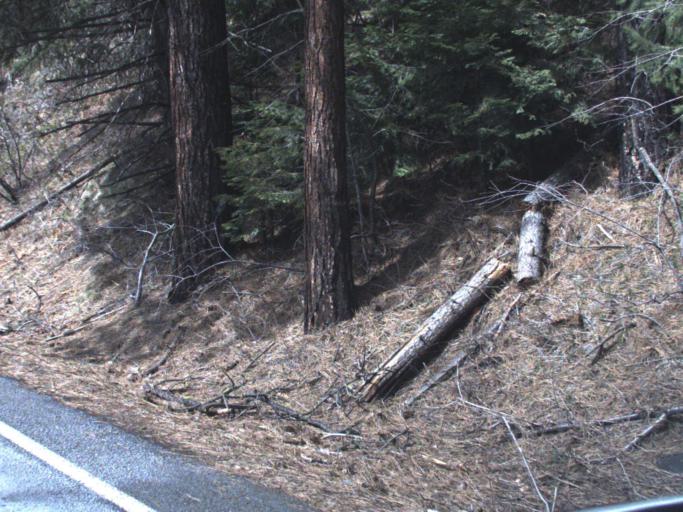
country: US
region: Washington
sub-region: Kittitas County
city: Cle Elum
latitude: 46.9783
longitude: -121.1665
